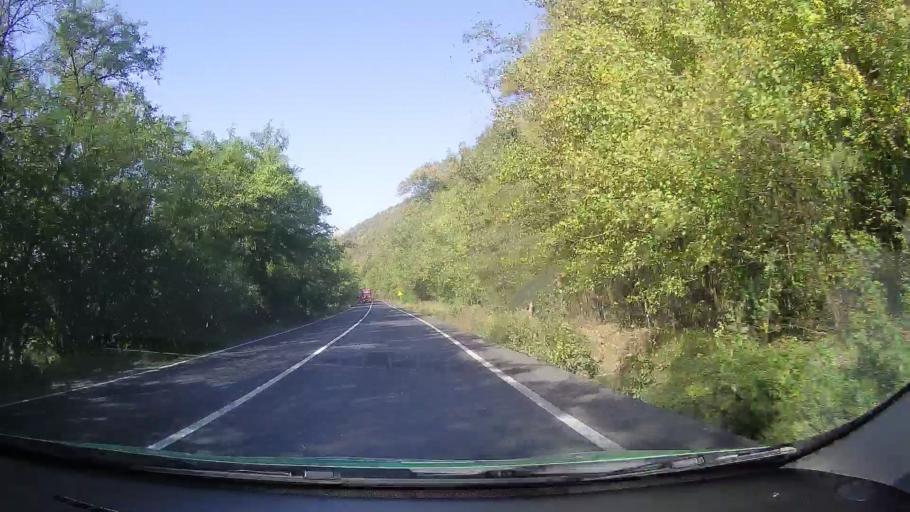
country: RO
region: Arad
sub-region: Comuna Savarsin
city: Savarsin
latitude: 46.0107
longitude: 22.2697
